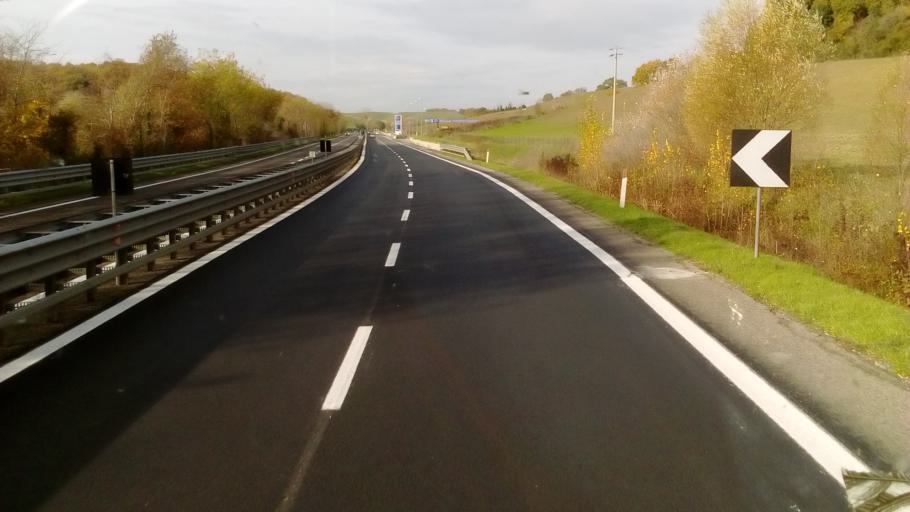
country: IT
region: Tuscany
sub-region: Provincia di Siena
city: Castelnuovo Berardenga
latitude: 43.3199
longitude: 11.4916
